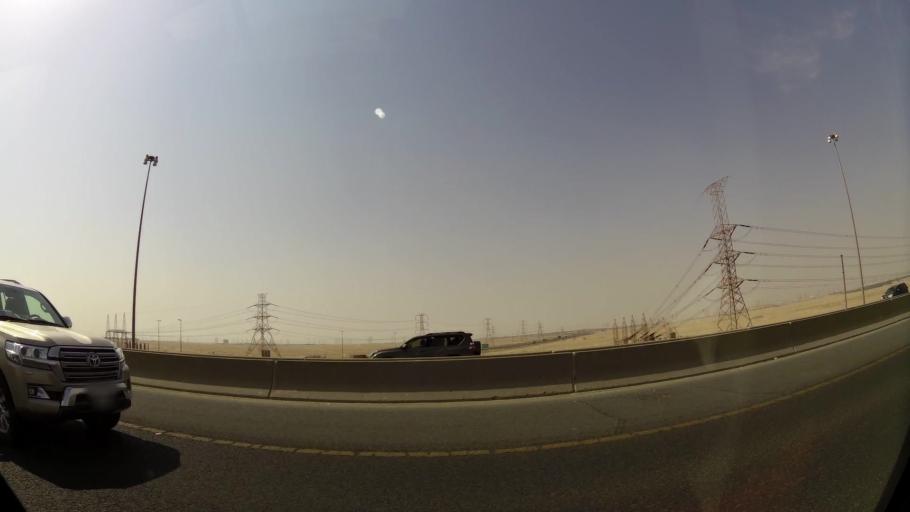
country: KW
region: Al Ahmadi
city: Al Fahahil
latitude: 29.0387
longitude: 48.1175
